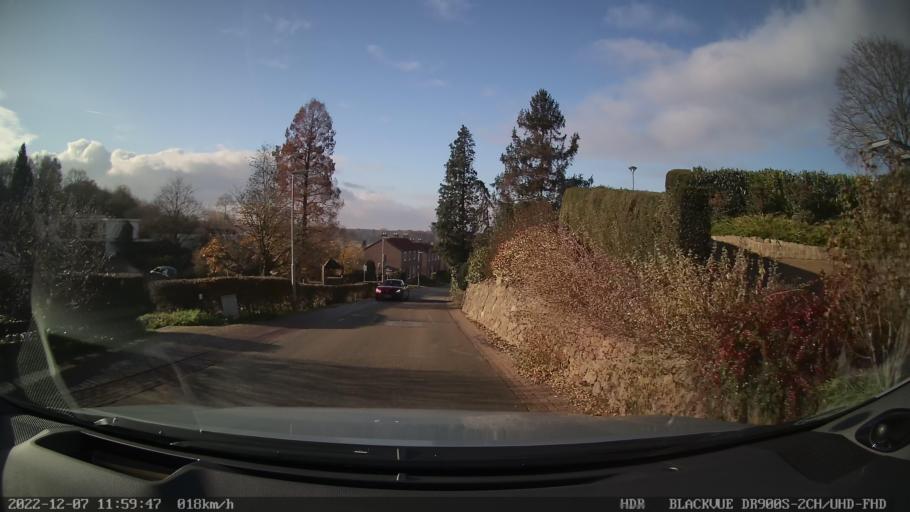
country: NL
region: Limburg
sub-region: Gemeente Schinnen
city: Puth
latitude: 50.9538
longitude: 5.8449
